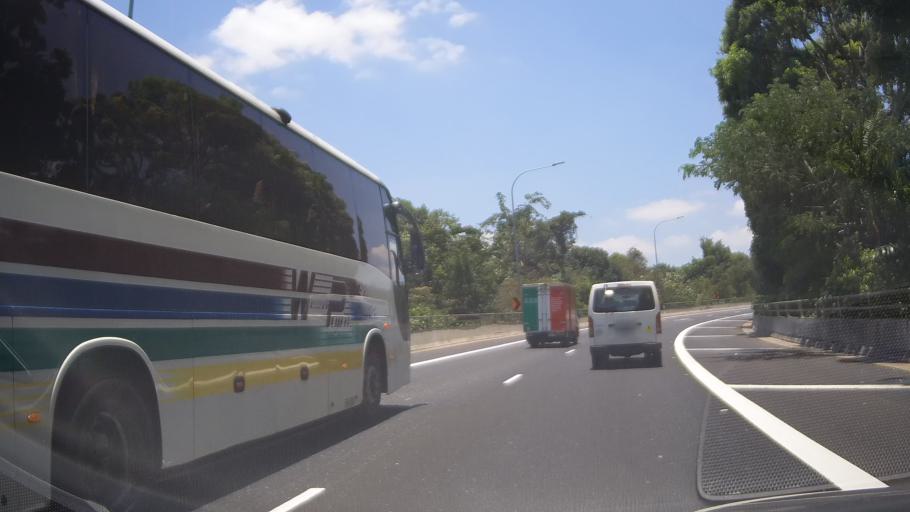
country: MY
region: Johor
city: Johor Bahru
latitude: 1.3932
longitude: 103.7752
